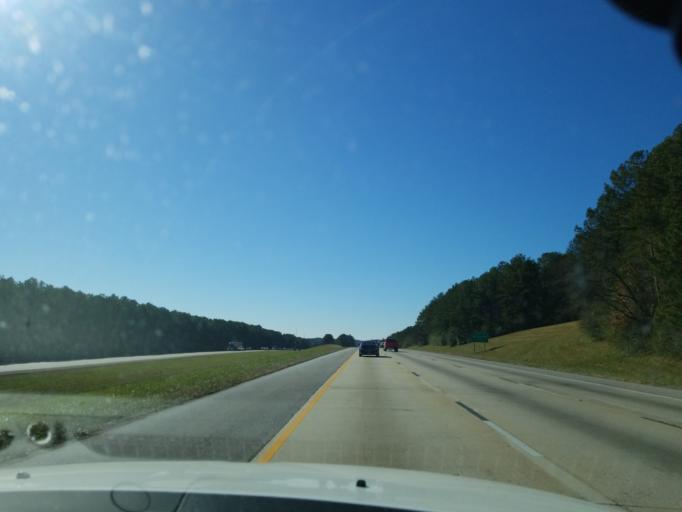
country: US
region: Alabama
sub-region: Jefferson County
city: Cahaba Heights
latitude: 33.4269
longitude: -86.7460
